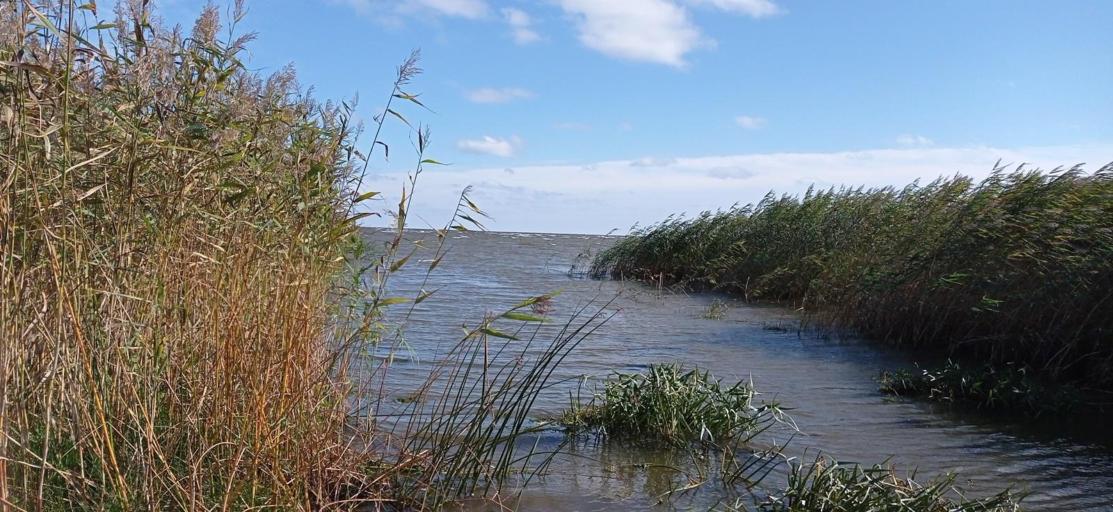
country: EE
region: Tartu
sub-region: Alatskivi vald
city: Kallaste
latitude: 58.5487
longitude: 27.2245
